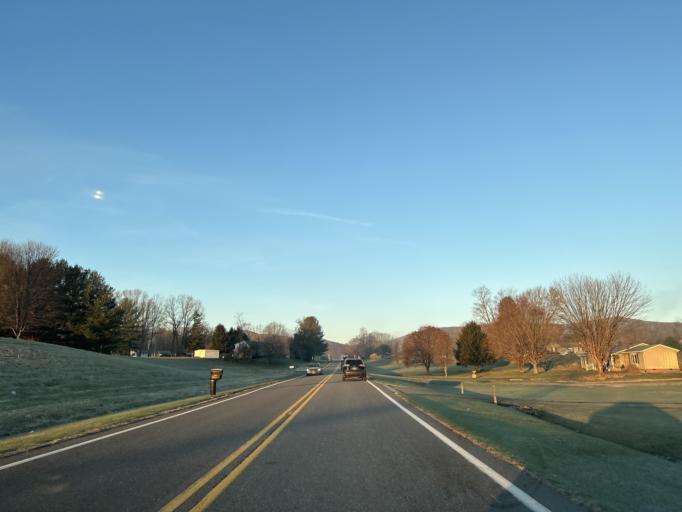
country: US
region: Virginia
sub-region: City of Staunton
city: Staunton
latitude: 38.2096
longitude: -79.1992
